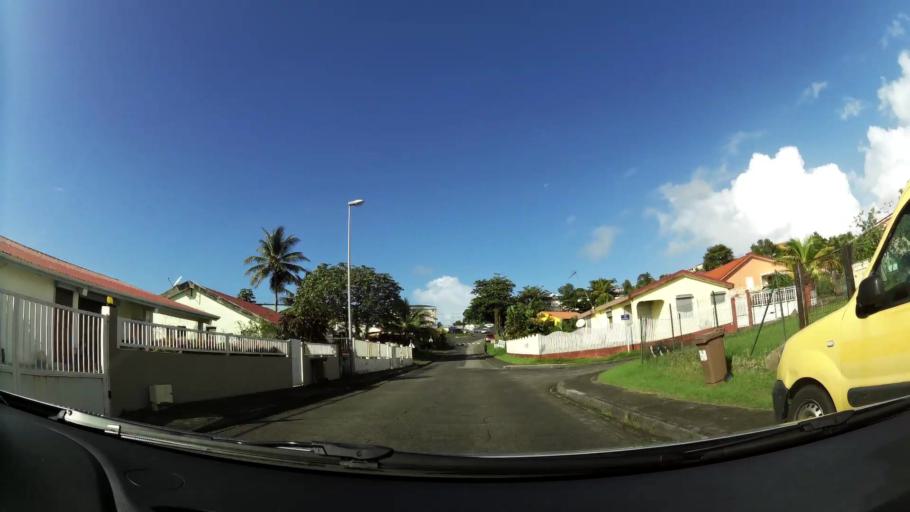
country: MQ
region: Martinique
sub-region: Martinique
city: Ducos
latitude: 14.5727
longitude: -60.9798
